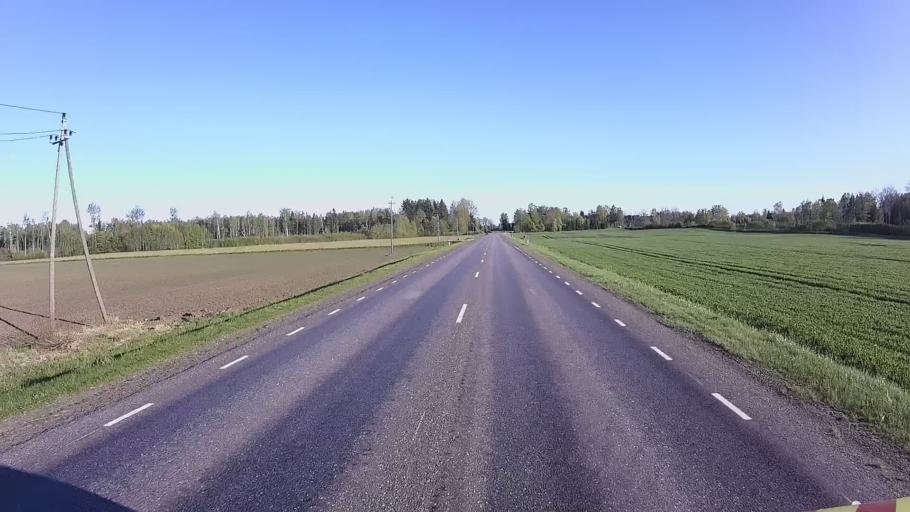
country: EE
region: Viljandimaa
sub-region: Viljandi linn
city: Viljandi
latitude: 58.4532
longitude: 25.5945
